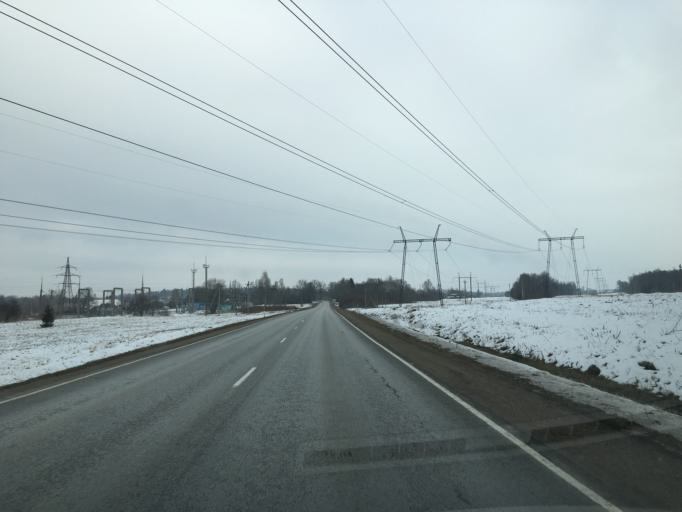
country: EE
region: Tartu
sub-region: Elva linn
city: Elva
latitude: 58.1324
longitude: 26.2452
